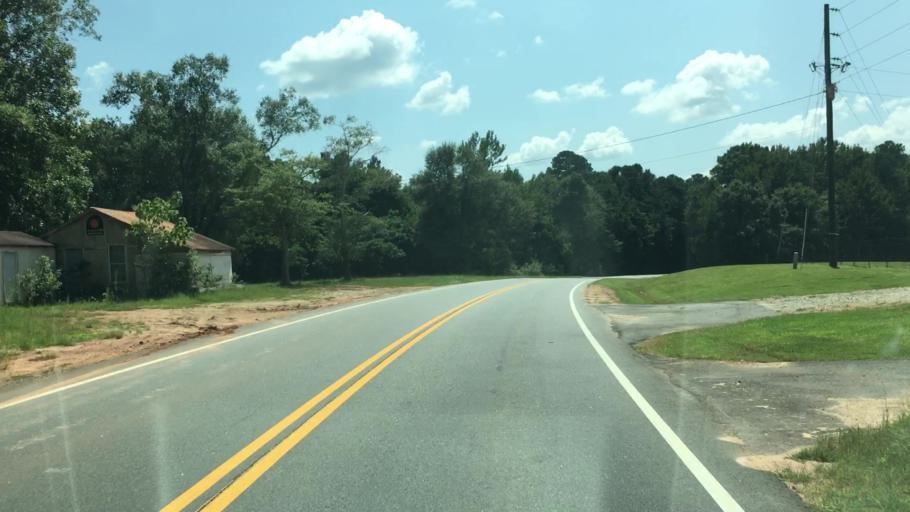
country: US
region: Georgia
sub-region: Oconee County
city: Watkinsville
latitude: 33.7722
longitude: -83.4279
